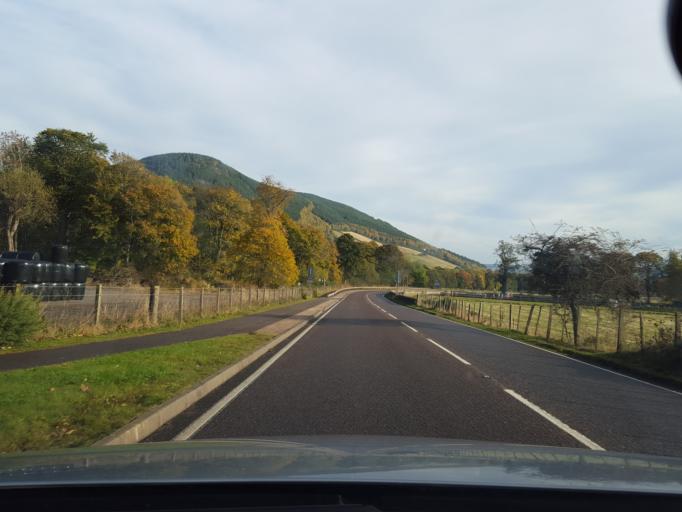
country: GB
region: Scotland
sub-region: Highland
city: Beauly
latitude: 57.3283
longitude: -4.4698
